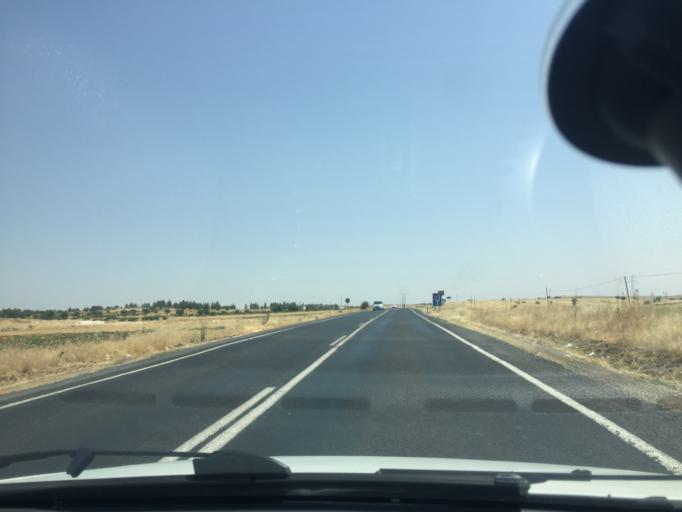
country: TR
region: Mardin
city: Acirli
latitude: 37.4417
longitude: 41.2905
